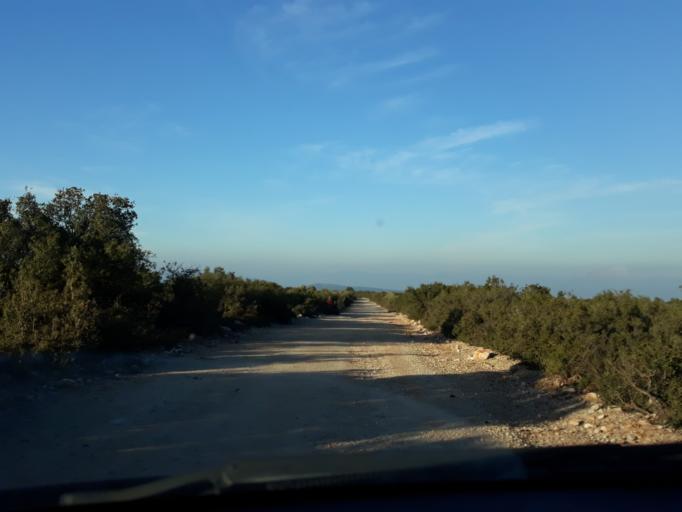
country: GR
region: Central Greece
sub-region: Nomos Voiotias
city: Ayios Thomas
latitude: 38.2405
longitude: 23.5335
